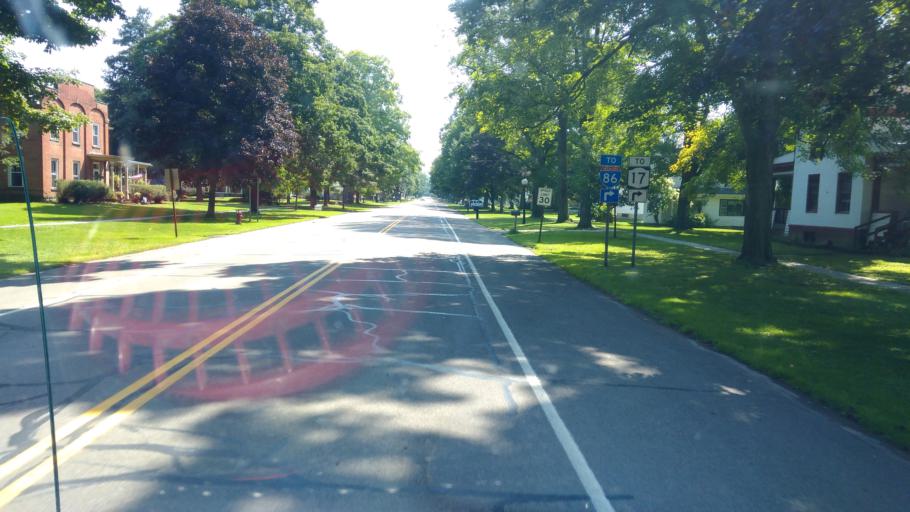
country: US
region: New York
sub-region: Allegany County
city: Belmont
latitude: 42.3054
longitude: -78.0137
